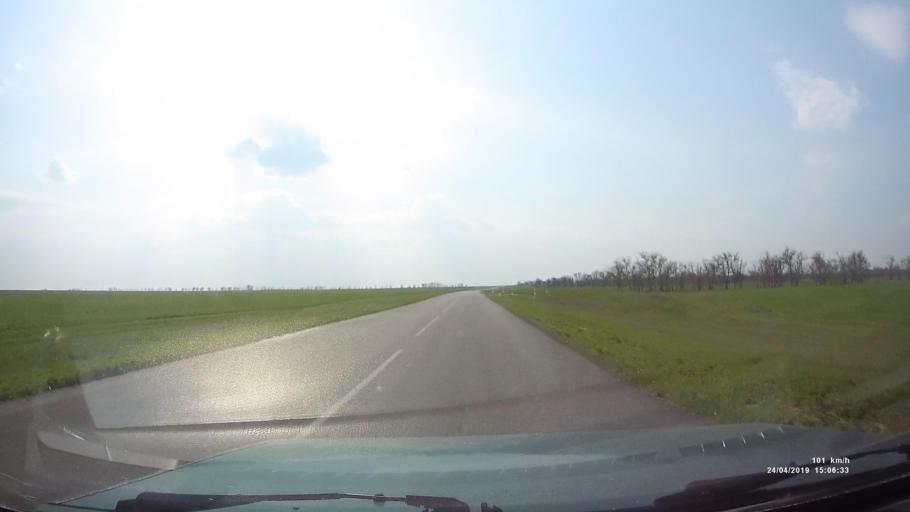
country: RU
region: Rostov
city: Remontnoye
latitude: 46.5588
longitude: 43.4247
